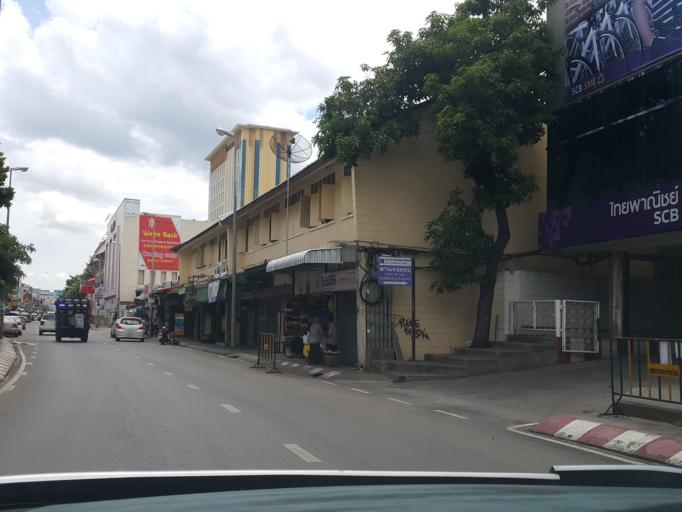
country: TH
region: Chiang Mai
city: Chiang Mai
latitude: 18.7874
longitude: 99.0010
